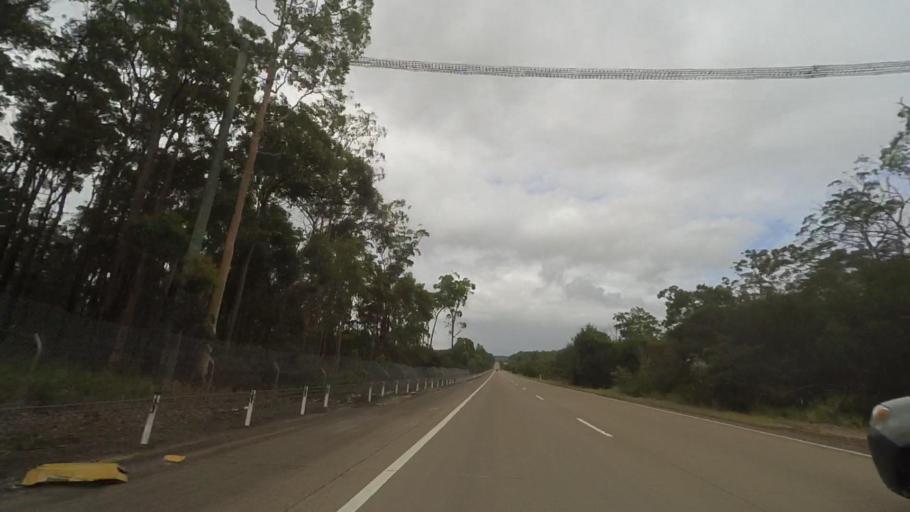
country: AU
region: New South Wales
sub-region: Port Stephens Shire
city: Medowie
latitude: -32.6393
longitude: 151.9317
